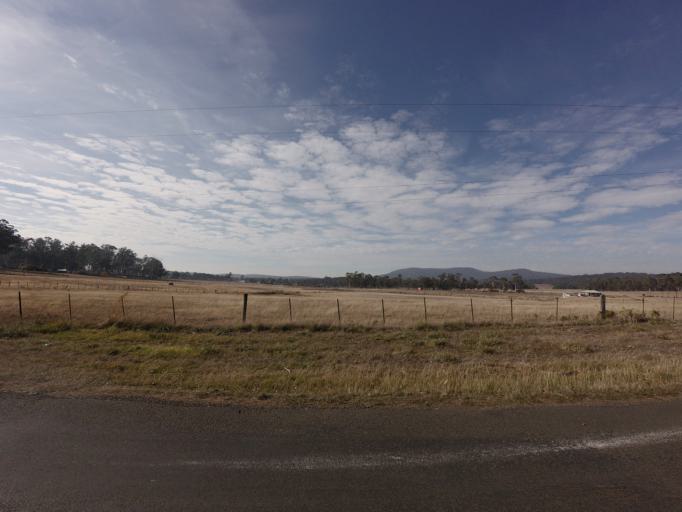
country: AU
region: Tasmania
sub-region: Sorell
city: Sorell
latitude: -42.4703
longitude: 147.4620
